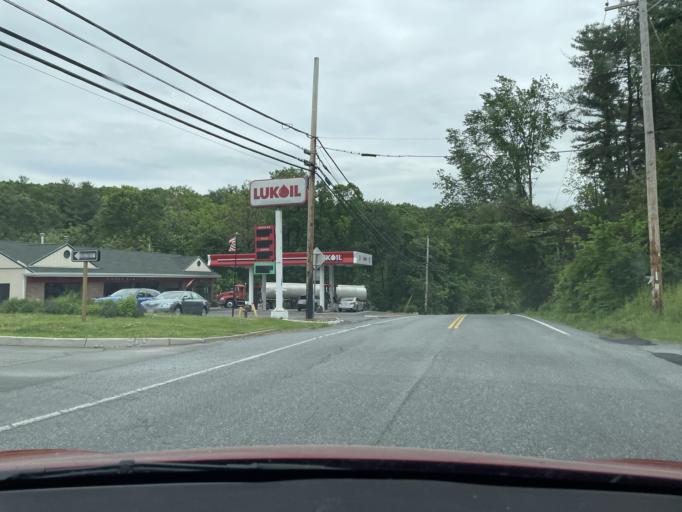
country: US
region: New York
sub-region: Ulster County
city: West Hurley
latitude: 42.0051
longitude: -74.1057
